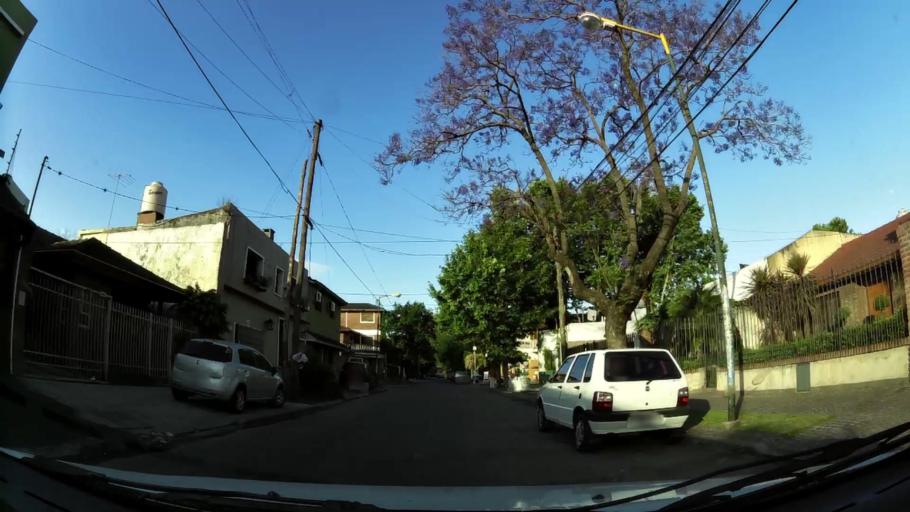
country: AR
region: Buenos Aires
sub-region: Partido de General San Martin
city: General San Martin
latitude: -34.5571
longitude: -58.5604
